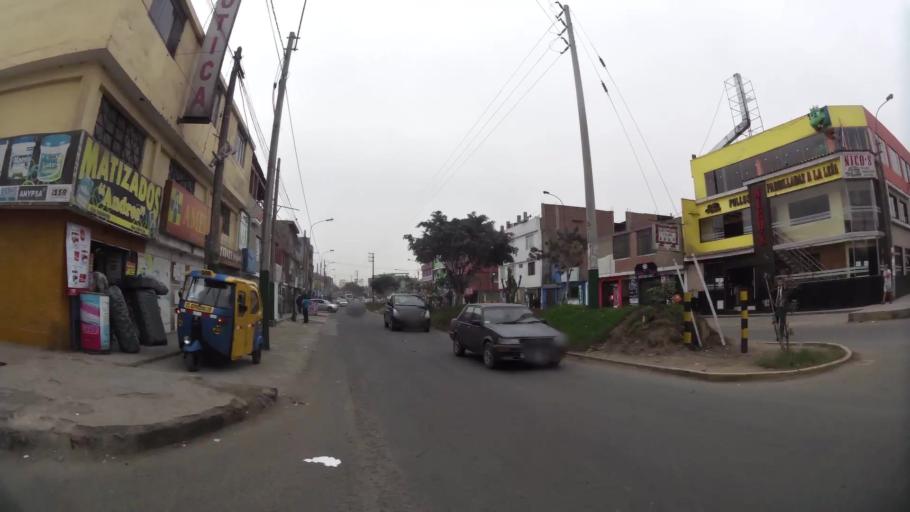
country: PE
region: Lima
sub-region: Lima
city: Surco
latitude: -12.1725
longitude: -76.9678
